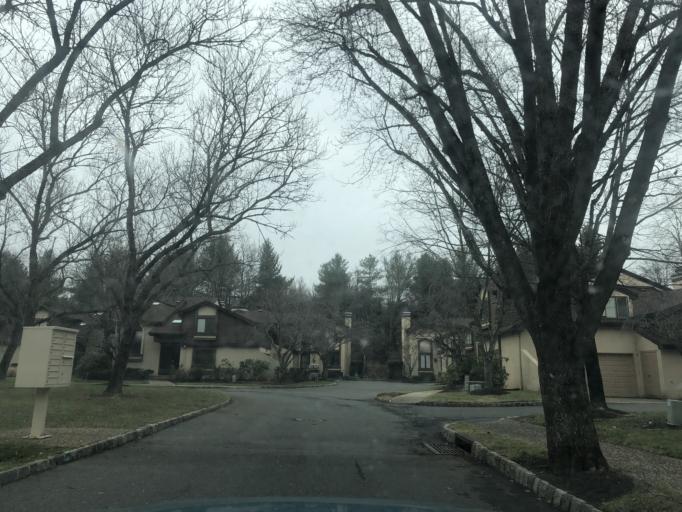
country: US
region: New Jersey
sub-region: Somerset County
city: Kingston
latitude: 40.3479
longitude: -74.6216
